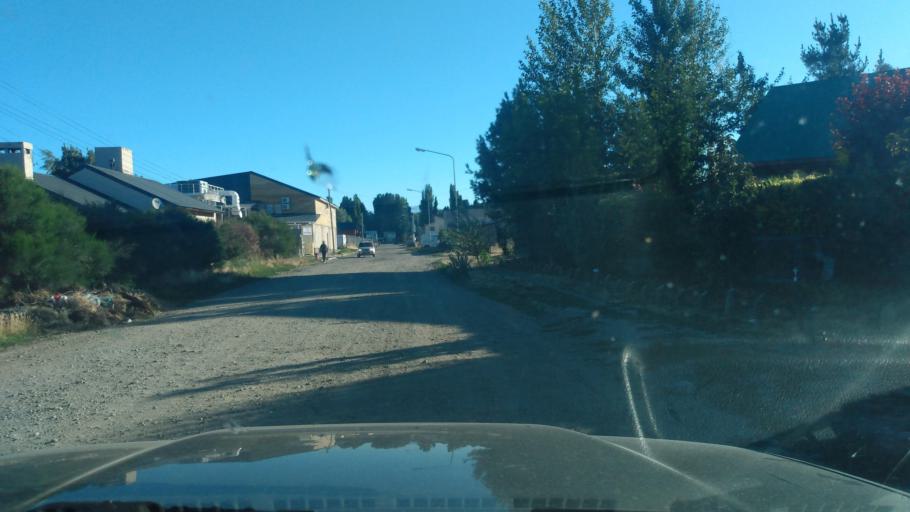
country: AR
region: Neuquen
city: Junin de los Andes
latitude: -39.9543
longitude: -71.0788
